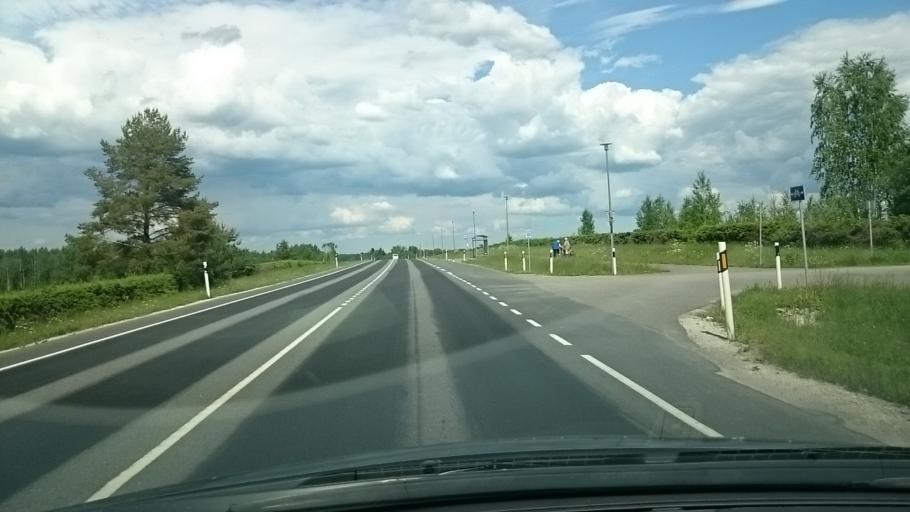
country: EE
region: Jaervamaa
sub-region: Tueri vald
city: Tueri
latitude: 58.8381
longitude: 25.4735
